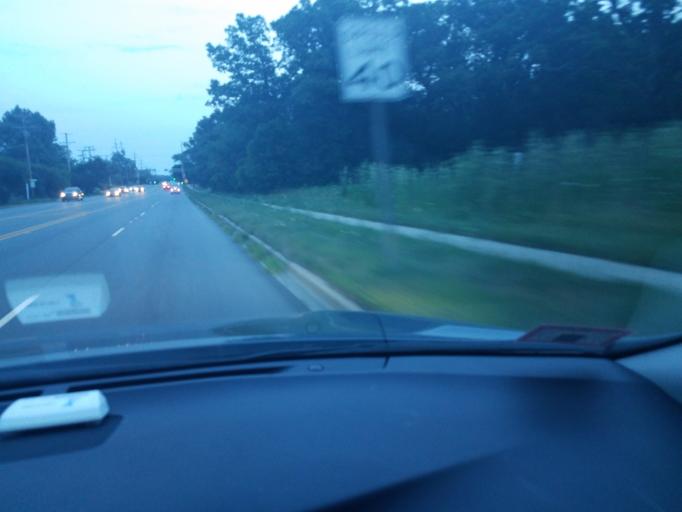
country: US
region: Illinois
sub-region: Cook County
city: Northbrook
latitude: 42.1380
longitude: -87.8020
